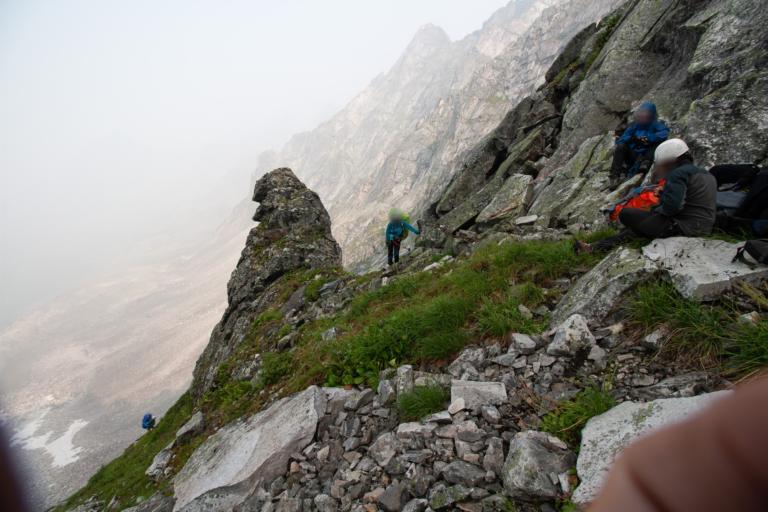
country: RU
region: Respublika Buryatiya
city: Novyy Uoyan
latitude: 56.2148
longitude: 110.9029
